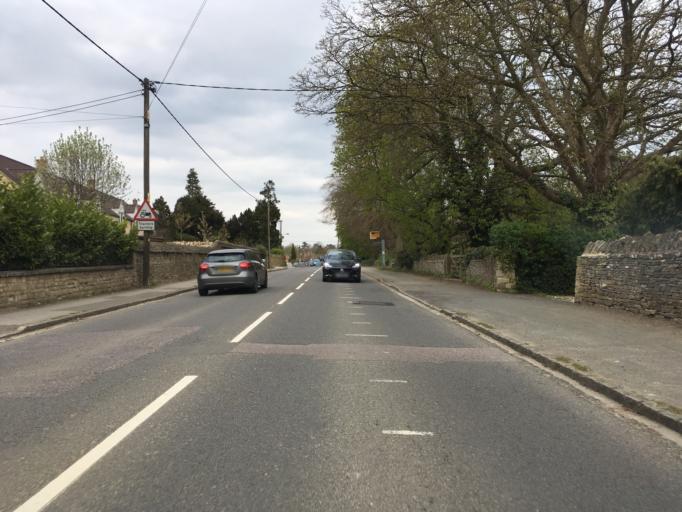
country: GB
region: England
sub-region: Oxfordshire
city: Woodstock
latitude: 51.8333
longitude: -1.3480
